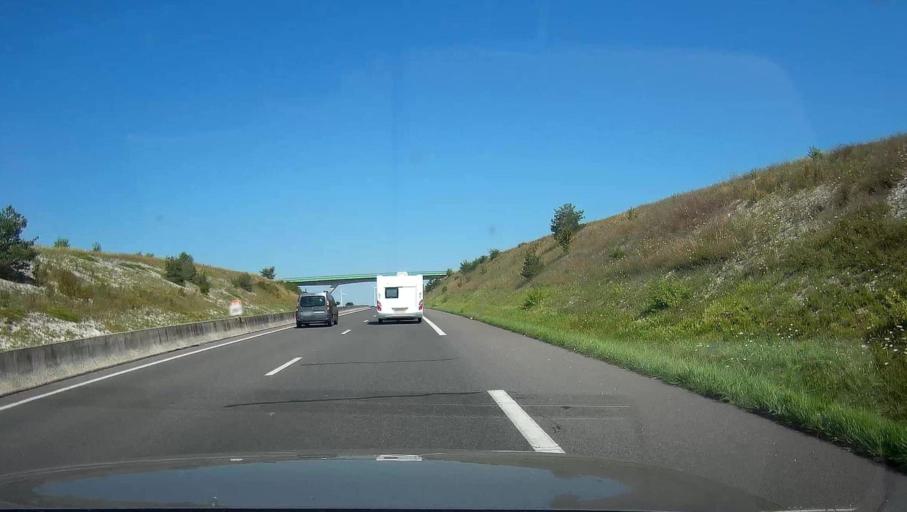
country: FR
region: Champagne-Ardenne
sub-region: Departement de l'Aube
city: Arcis-sur-Aube
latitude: 48.5548
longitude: 4.1938
